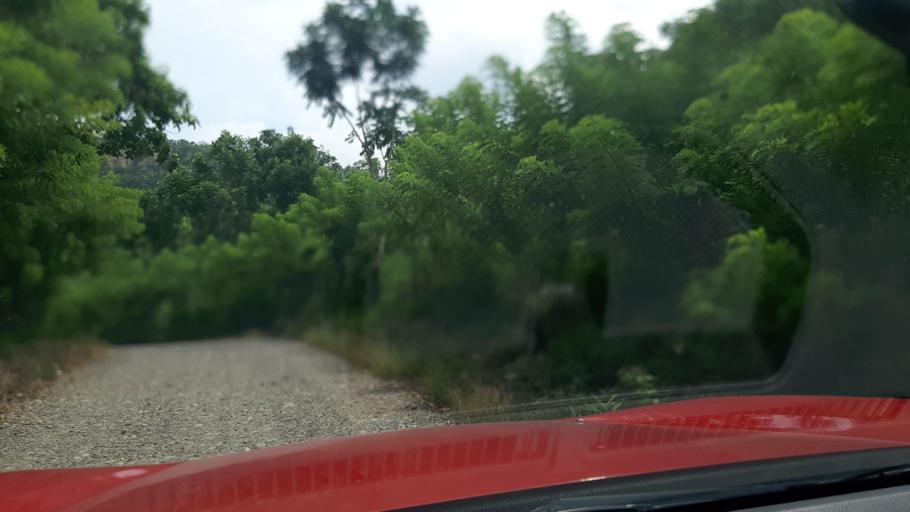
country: MX
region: Veracruz
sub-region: Papantla
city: Polutla
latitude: 20.4622
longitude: -97.1864
